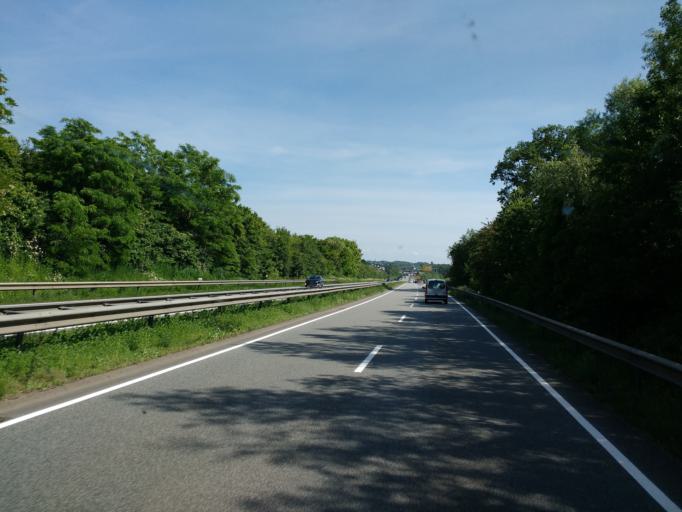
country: DE
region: North Rhine-Westphalia
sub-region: Regierungsbezirk Detmold
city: Herford
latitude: 52.1103
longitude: 8.6454
